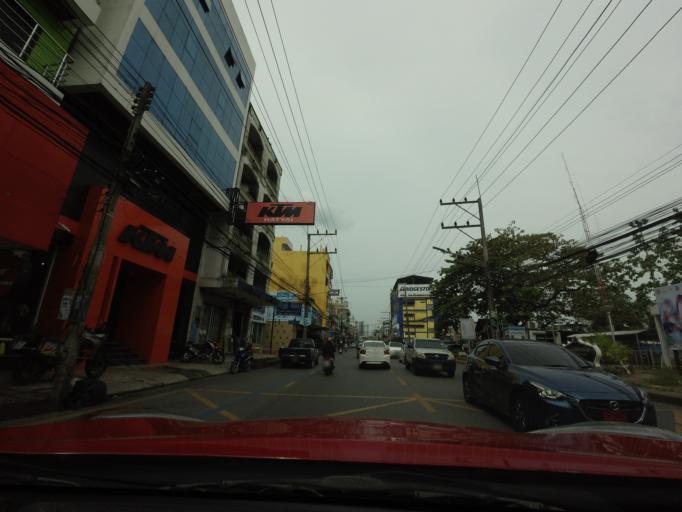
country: TH
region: Songkhla
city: Hat Yai
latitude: 6.9980
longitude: 100.4725
